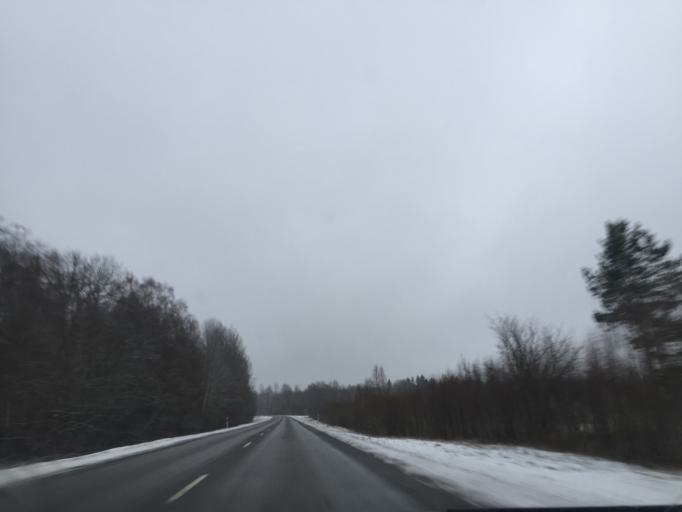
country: EE
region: Laeaene
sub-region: Lihula vald
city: Lihula
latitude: 58.5542
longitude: 23.9869
